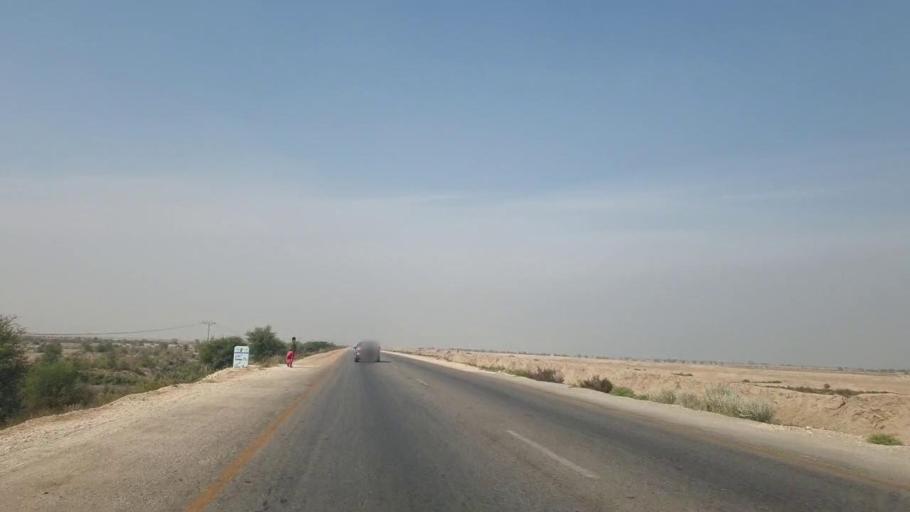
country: PK
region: Sindh
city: Sann
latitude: 25.9057
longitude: 68.2288
